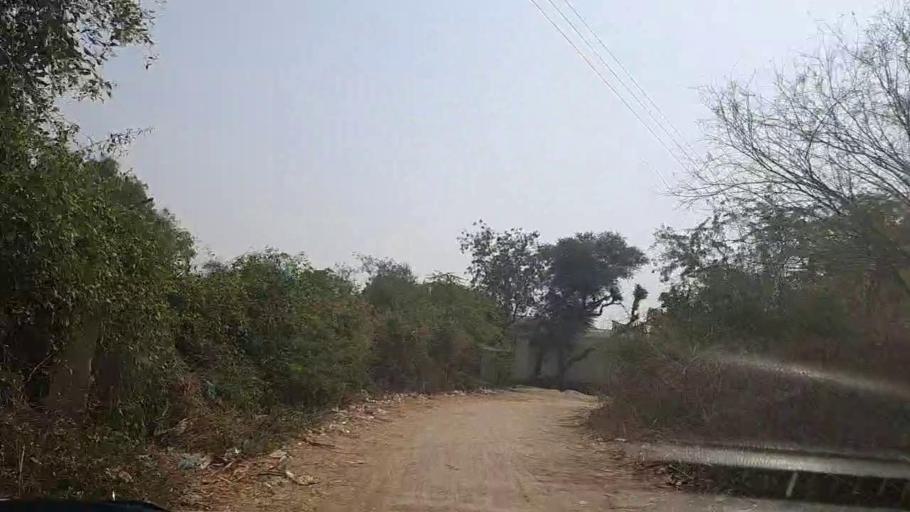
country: PK
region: Sindh
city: Pithoro
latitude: 25.5475
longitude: 69.2500
